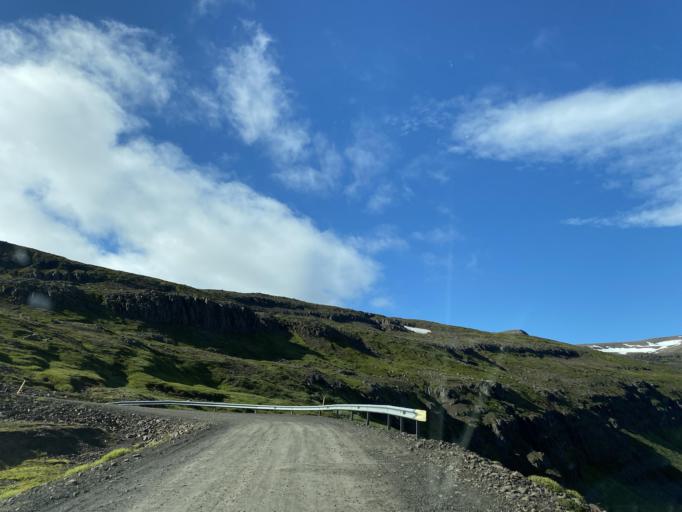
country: IS
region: East
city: Eskifjoerdur
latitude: 65.1801
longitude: -14.0865
